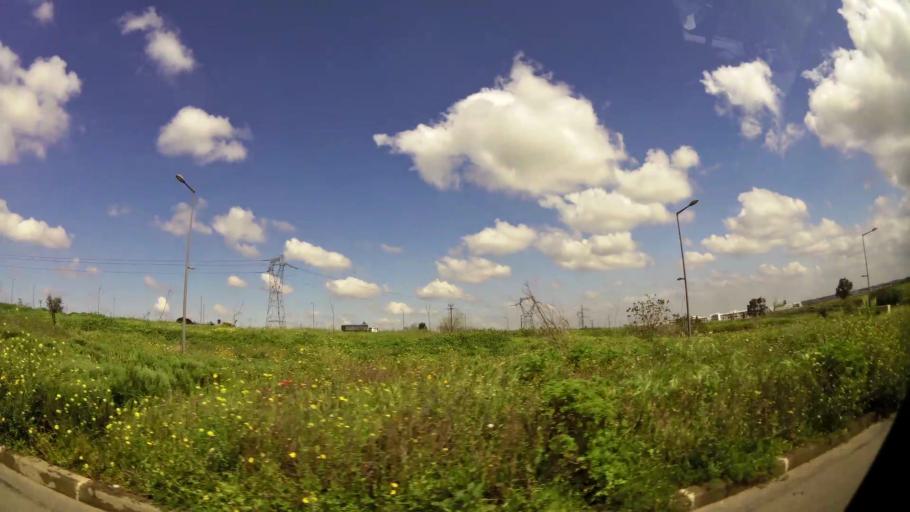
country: MA
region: Grand Casablanca
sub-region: Nouaceur
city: Bouskoura
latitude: 33.4988
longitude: -7.6085
